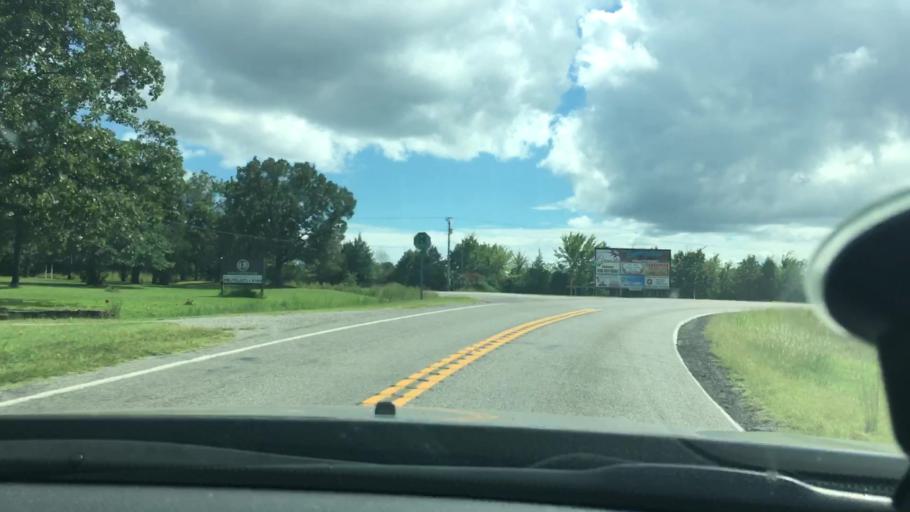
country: US
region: Oklahoma
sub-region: Sequoyah County
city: Vian
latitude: 35.6108
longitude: -94.9649
